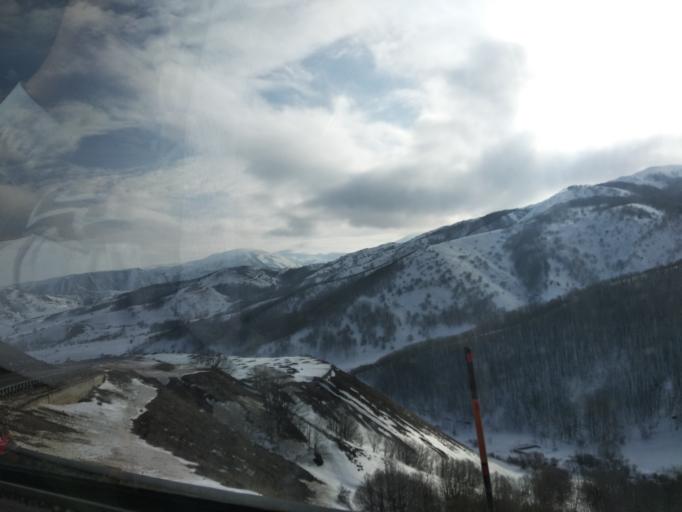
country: TR
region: Erzincan
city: Catalarmut
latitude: 39.8971
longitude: 39.3900
